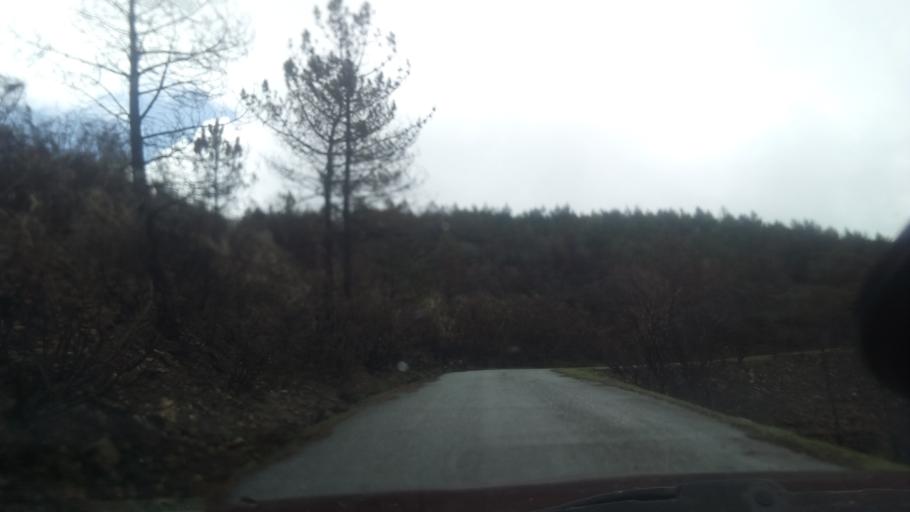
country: PT
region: Guarda
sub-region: Celorico da Beira
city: Celorico da Beira
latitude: 40.5392
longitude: -7.4451
